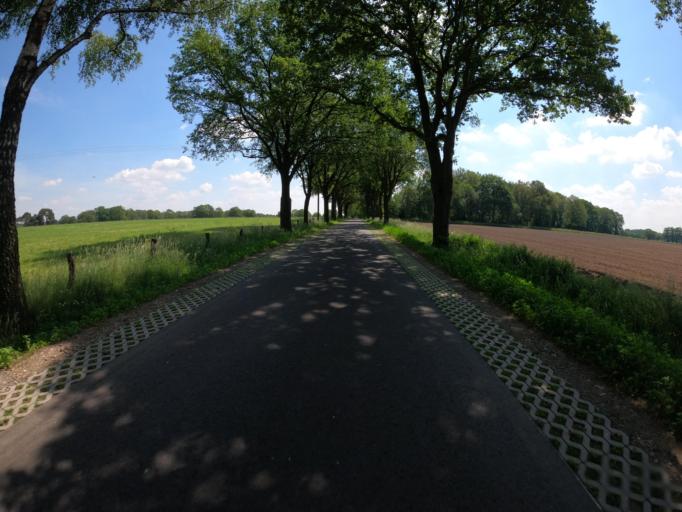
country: DE
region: North Rhine-Westphalia
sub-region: Regierungsbezirk Dusseldorf
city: Hunxe
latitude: 51.6977
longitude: 6.8070
